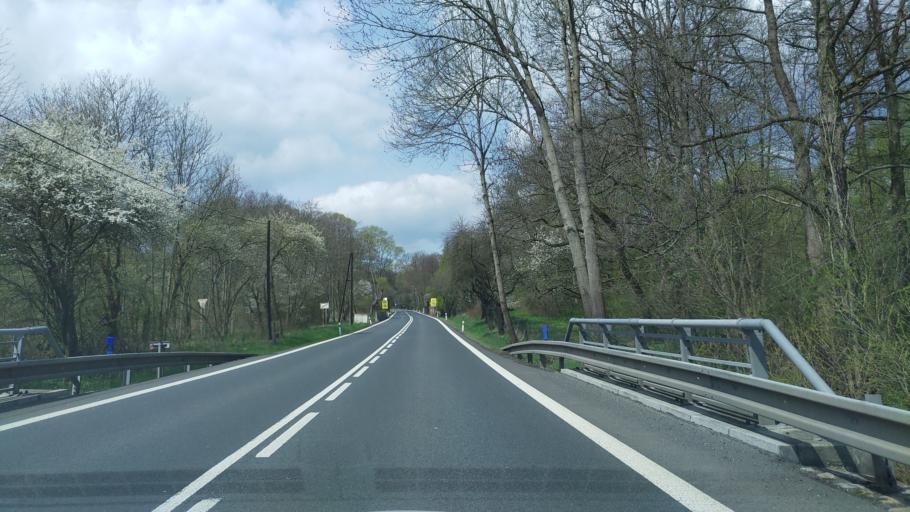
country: CZ
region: Karlovarsky
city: Ostrov
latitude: 50.3326
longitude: 13.0094
